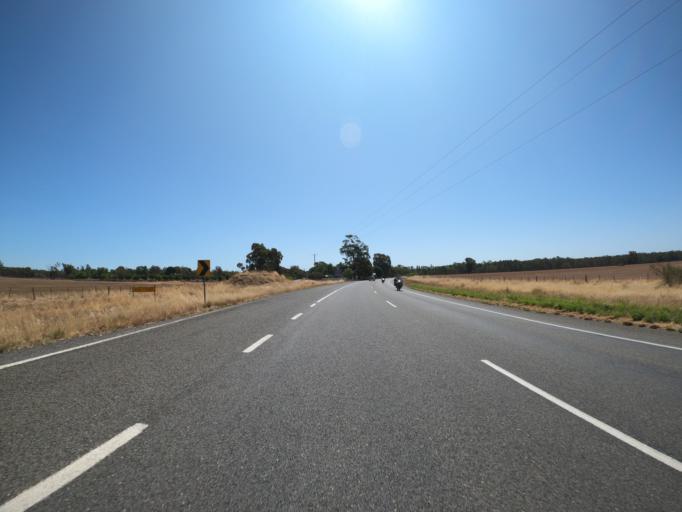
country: AU
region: New South Wales
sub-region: Corowa Shire
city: Corowa
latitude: -36.0702
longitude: 146.2095
